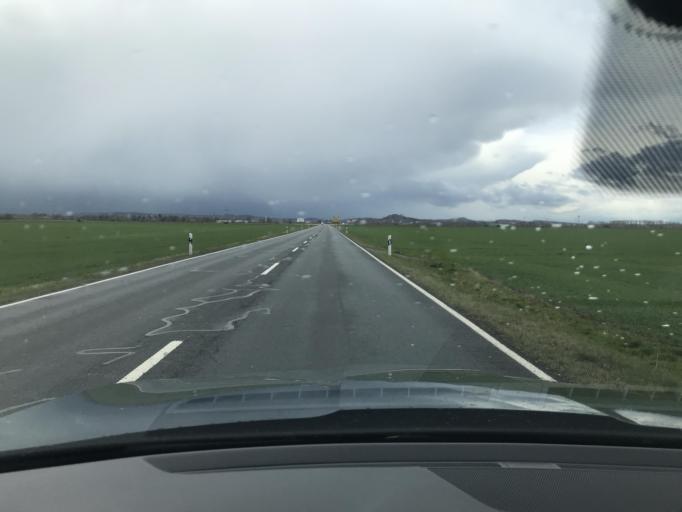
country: DE
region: Saxony-Anhalt
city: Quedlinburg
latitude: 51.7900
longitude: 11.1905
